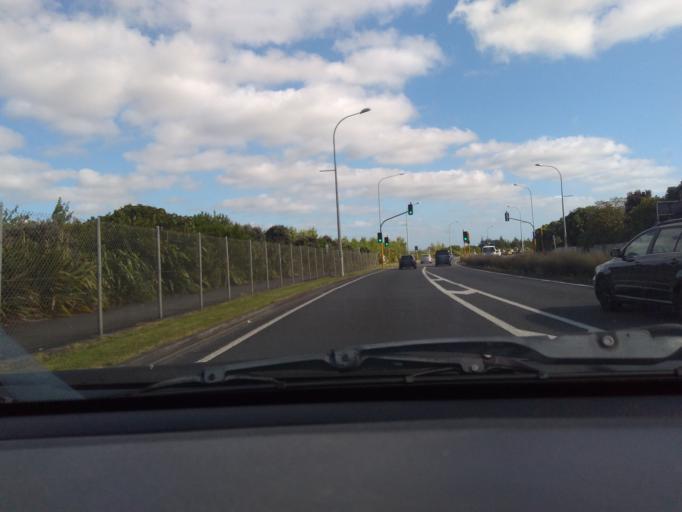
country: NZ
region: Auckland
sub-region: Auckland
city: Manukau City
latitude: -36.9501
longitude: 174.8596
